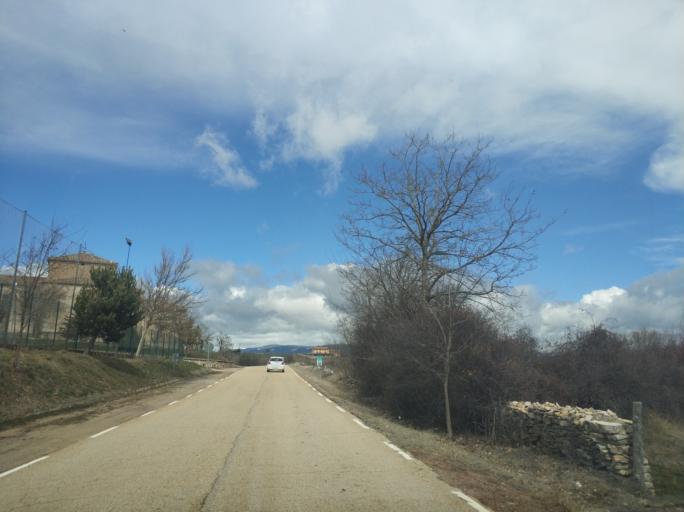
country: ES
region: Castille and Leon
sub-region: Provincia de Soria
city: Abejar
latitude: 41.8030
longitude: -2.7810
